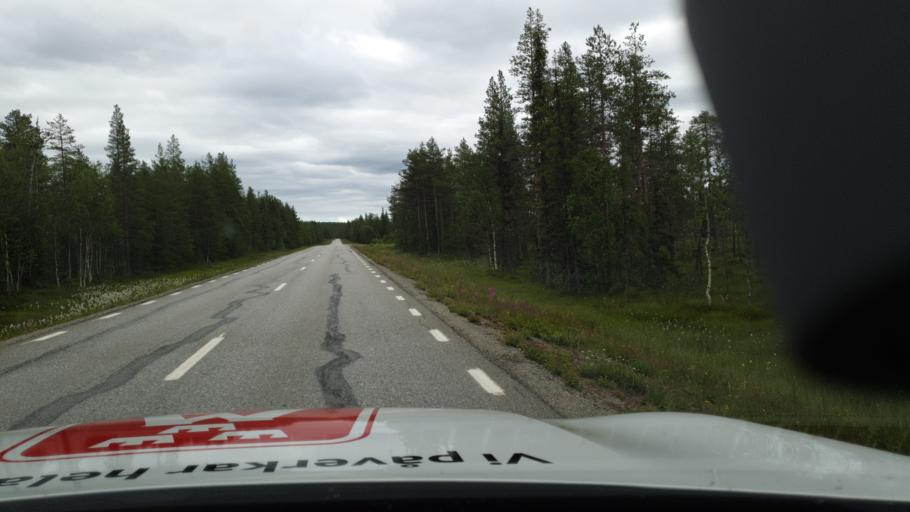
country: SE
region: Vaesterbotten
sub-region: Lycksele Kommun
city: Soderfors
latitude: 64.6933
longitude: 17.7600
